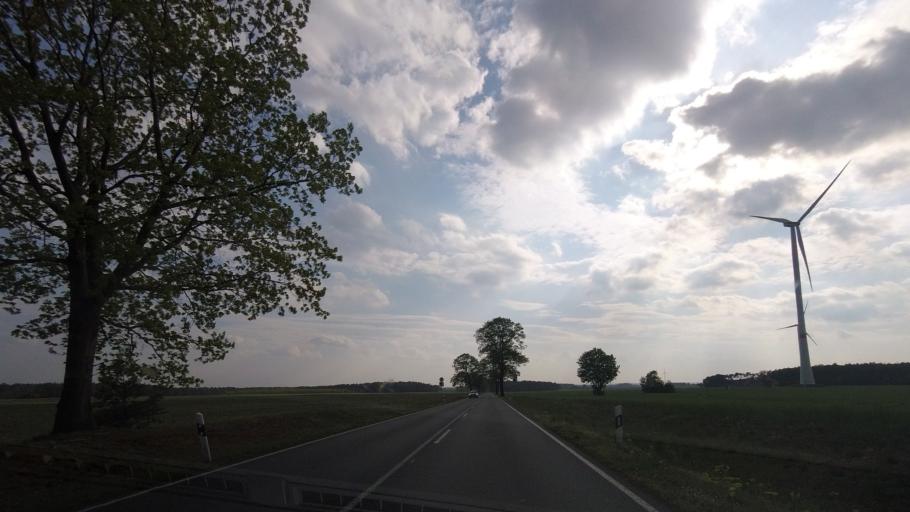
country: DE
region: Brandenburg
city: Luckau
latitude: 51.8796
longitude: 13.7711
